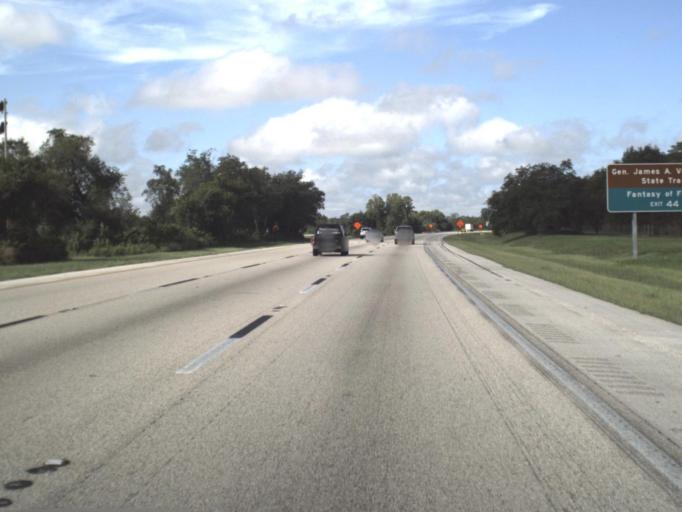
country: US
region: Florida
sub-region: Polk County
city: Polk City
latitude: 28.1635
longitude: -81.7799
